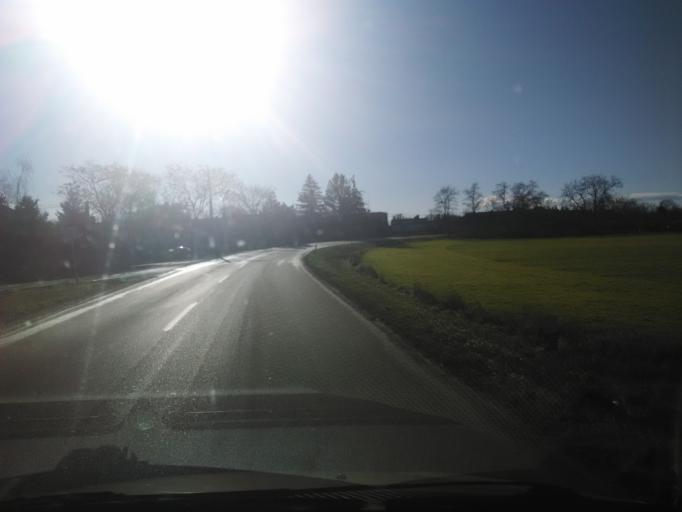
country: SK
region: Nitriansky
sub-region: Okres Nitra
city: Vrable
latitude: 48.2391
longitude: 18.2896
